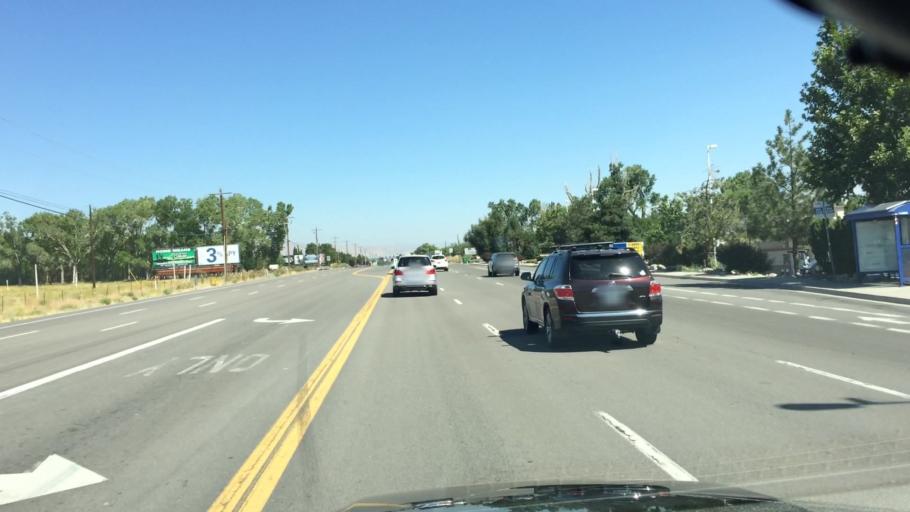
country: US
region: Nevada
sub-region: Washoe County
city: Sparks
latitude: 39.4217
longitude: -119.7584
